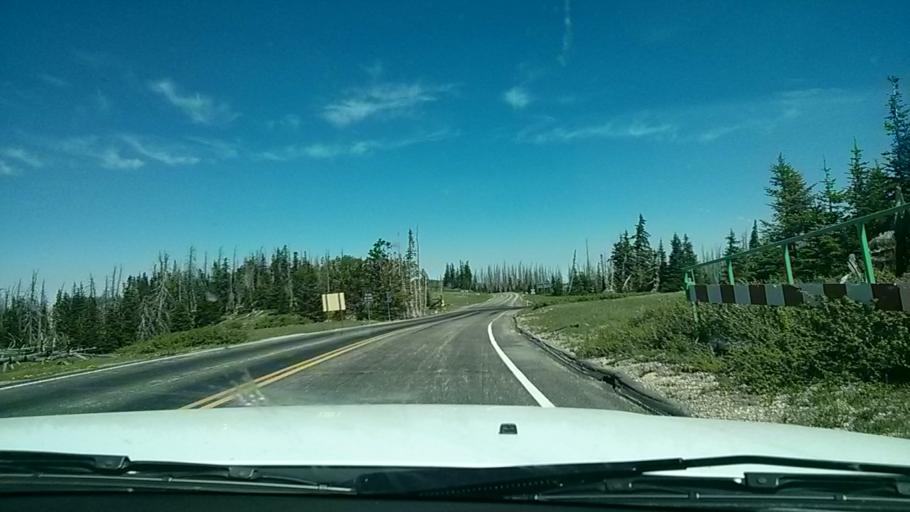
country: US
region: Utah
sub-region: Iron County
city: Parowan
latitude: 37.6535
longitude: -112.8252
